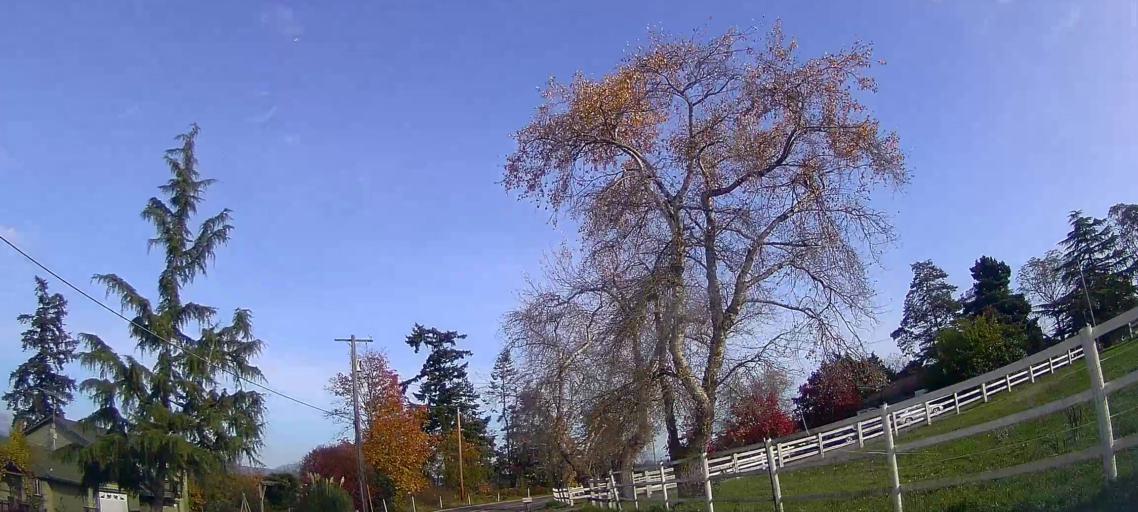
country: US
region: Washington
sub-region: Snohomish County
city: Stanwood
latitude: 48.2543
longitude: -122.4238
